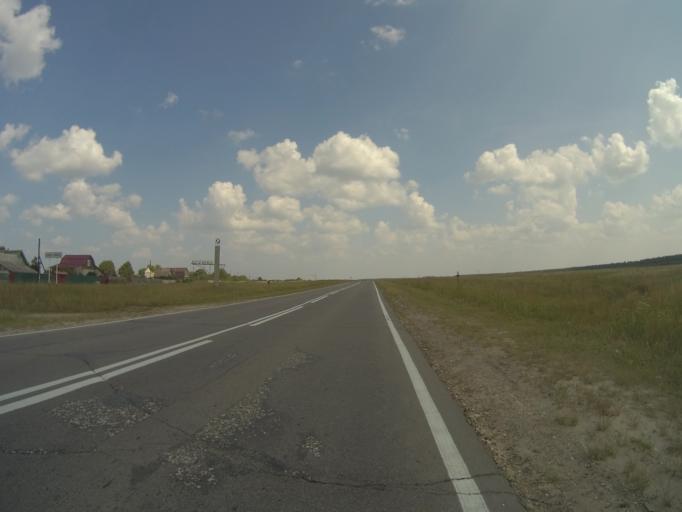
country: RU
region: Vladimir
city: Anopino
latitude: 55.6340
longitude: 40.7993
